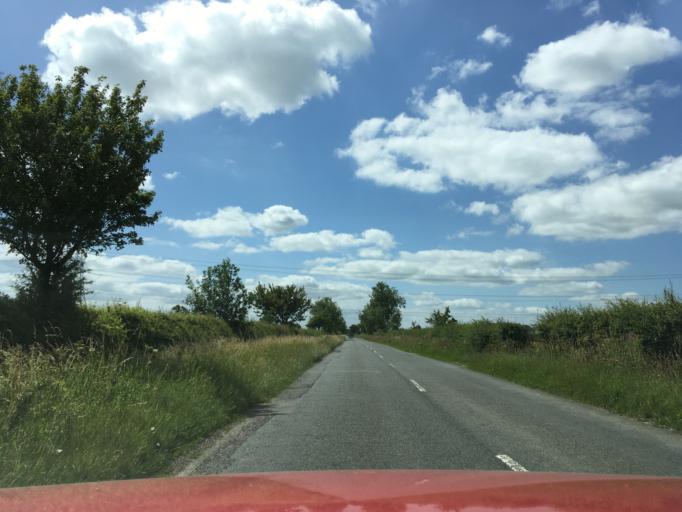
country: GB
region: England
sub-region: Buckinghamshire
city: Winslow
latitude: 51.9276
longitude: -0.8360
